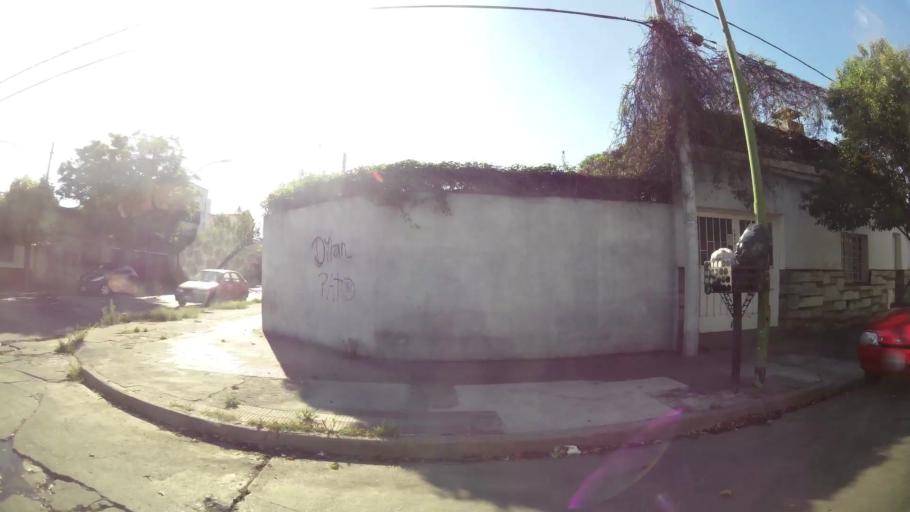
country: AR
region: Cordoba
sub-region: Departamento de Capital
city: Cordoba
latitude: -31.3905
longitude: -64.1673
